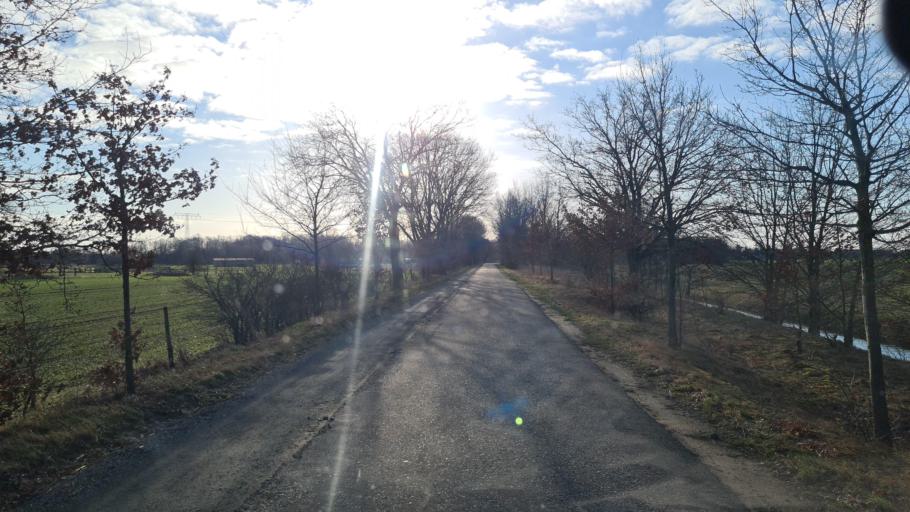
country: DE
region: Brandenburg
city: Herzberg
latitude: 51.7080
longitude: 13.2114
